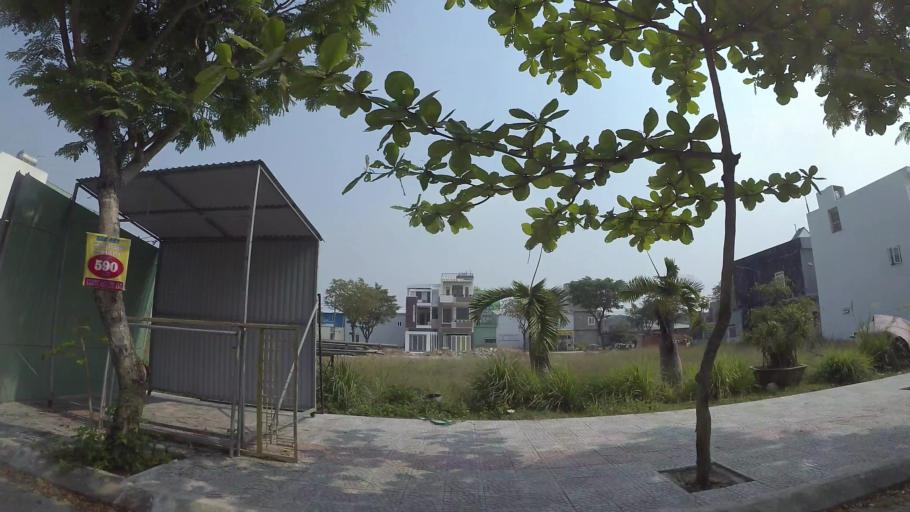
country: VN
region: Da Nang
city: Cam Le
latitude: 16.0029
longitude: 108.2239
